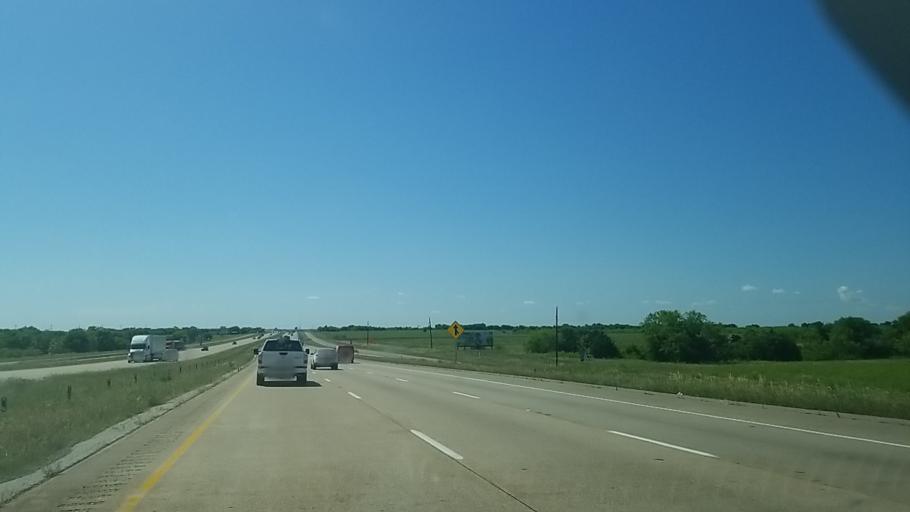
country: US
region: Texas
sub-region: Ellis County
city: Ennis
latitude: 32.2877
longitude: -96.5473
